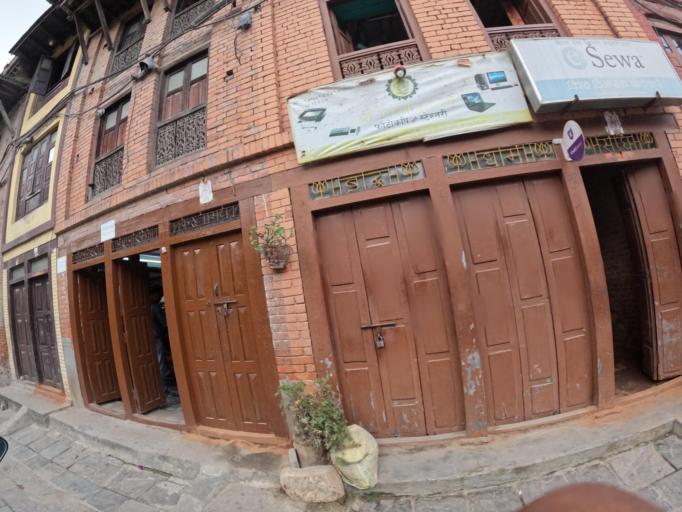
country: NP
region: Central Region
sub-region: Bagmati Zone
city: Bhaktapur
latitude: 27.6820
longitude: 85.3866
